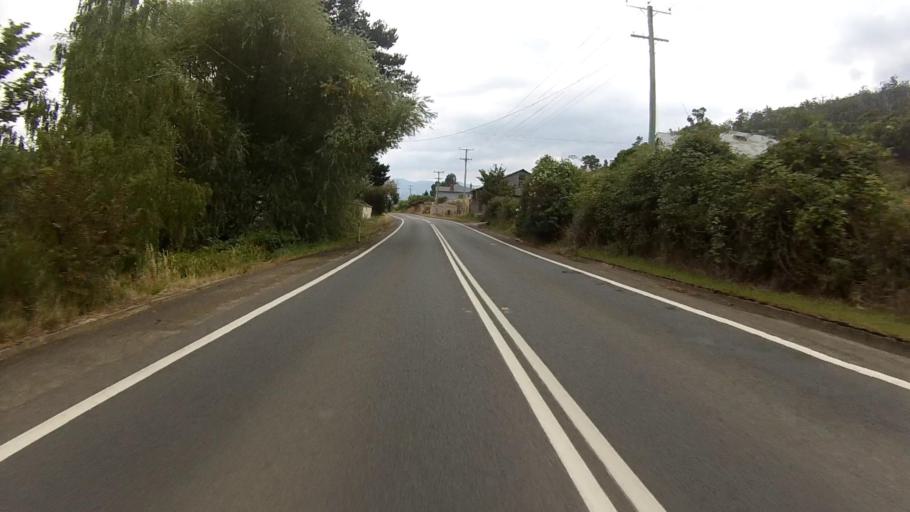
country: AU
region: Tasmania
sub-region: Huon Valley
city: Huonville
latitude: -43.0494
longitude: 147.0504
